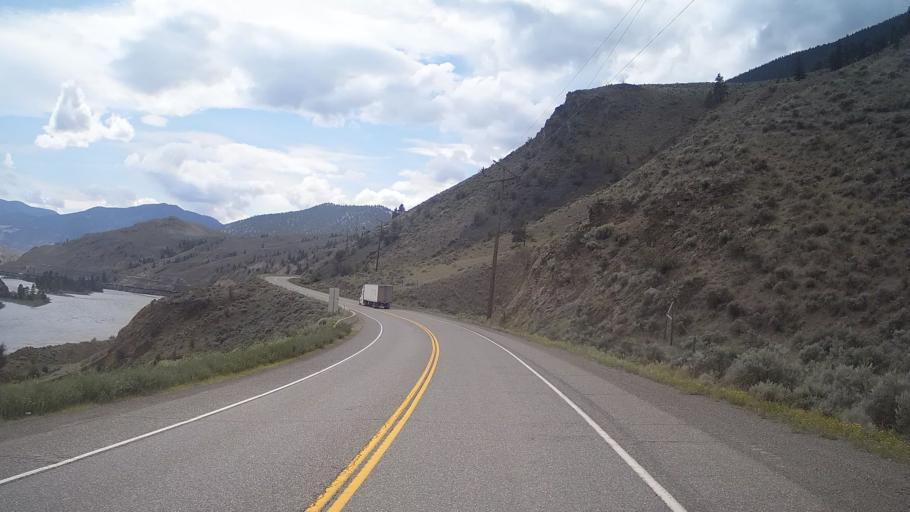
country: CA
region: British Columbia
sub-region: Thompson-Nicola Regional District
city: Ashcroft
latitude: 50.4945
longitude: -121.2947
